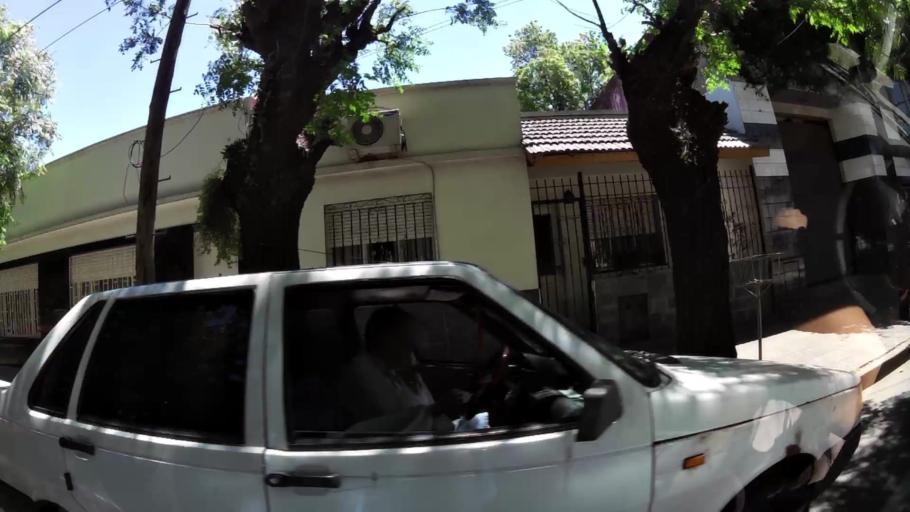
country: AR
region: Buenos Aires
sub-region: Partido de General San Martin
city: General San Martin
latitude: -34.5974
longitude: -58.5312
